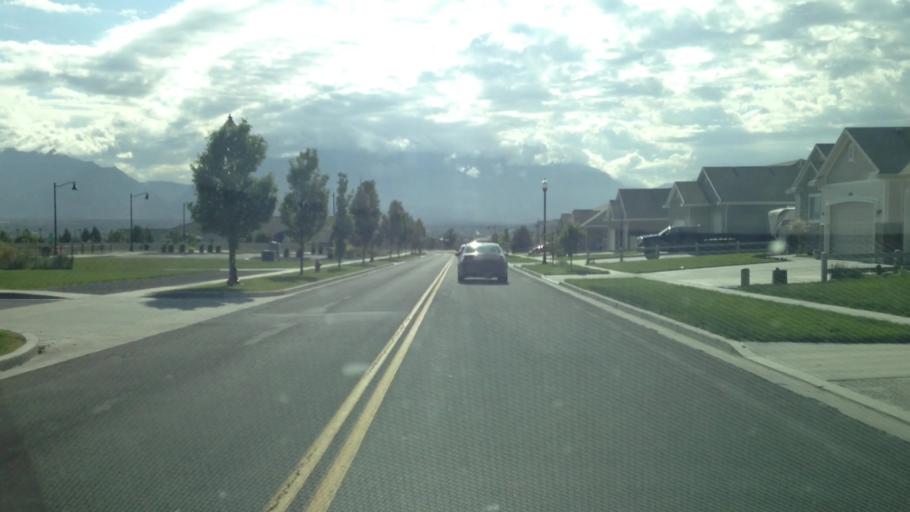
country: US
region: Utah
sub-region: Utah County
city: Saratoga Springs
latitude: 40.3916
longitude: -111.9284
